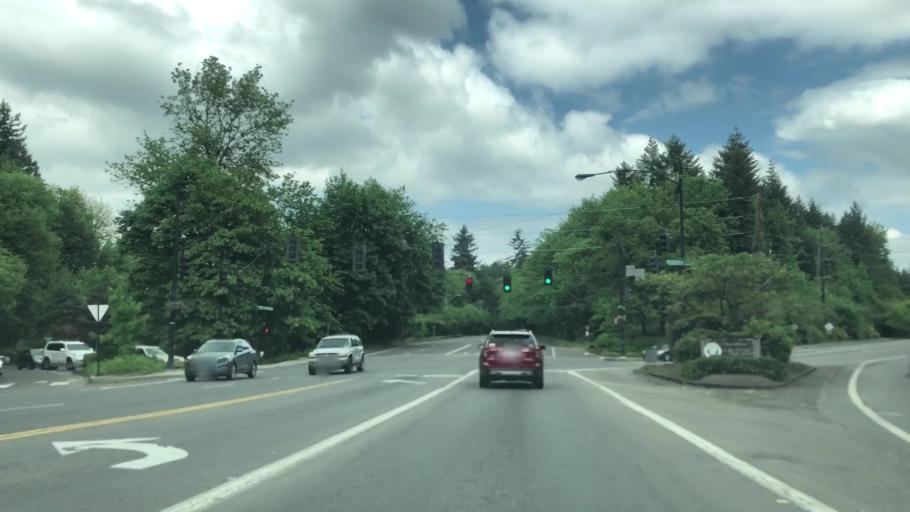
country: US
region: Oregon
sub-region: Clackamas County
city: Lake Oswego
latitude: 45.4241
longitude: -122.7081
